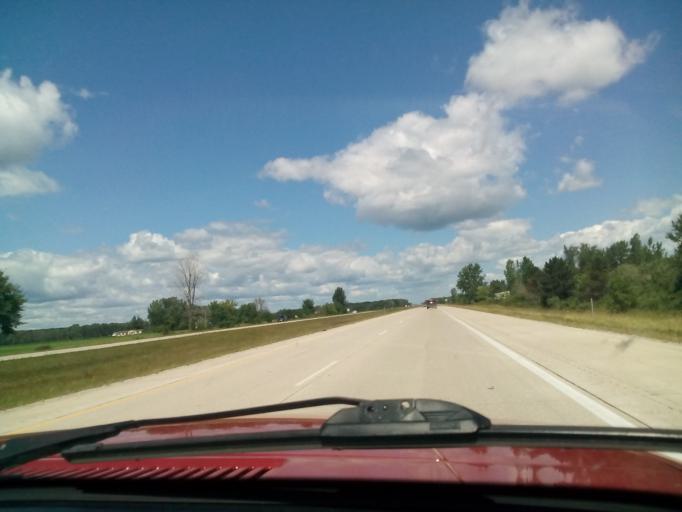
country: US
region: Michigan
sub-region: Bay County
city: Pinconning
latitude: 43.8072
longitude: -84.0206
